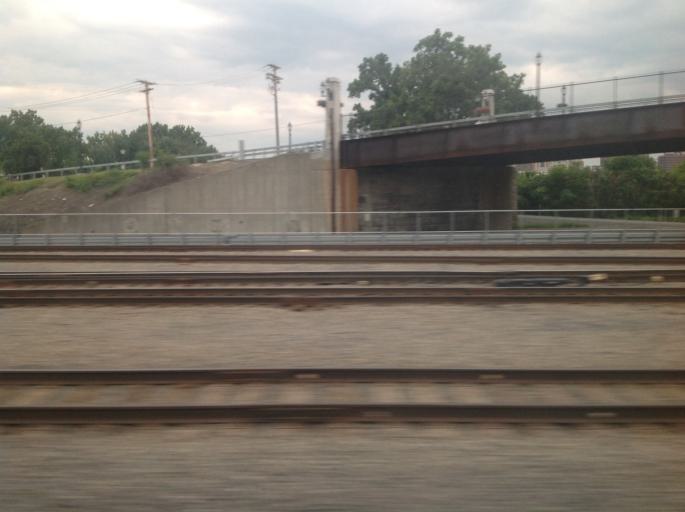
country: US
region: New York
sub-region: Rensselaer County
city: Rensselaer
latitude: 42.6447
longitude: -73.7408
